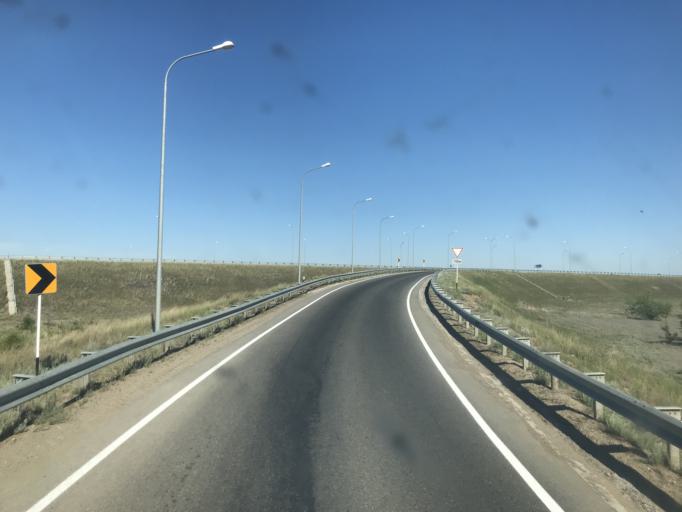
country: KZ
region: Aqtoebe
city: Aqtobe
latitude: 50.2944
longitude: 57.4384
